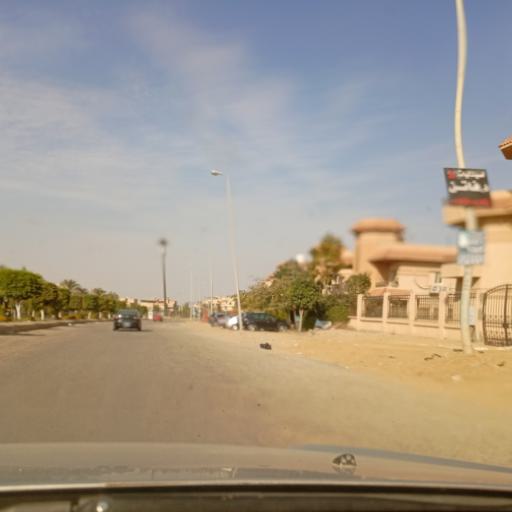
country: EG
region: Muhafazat al Qalyubiyah
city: Al Khankah
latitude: 30.0514
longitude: 31.4853
